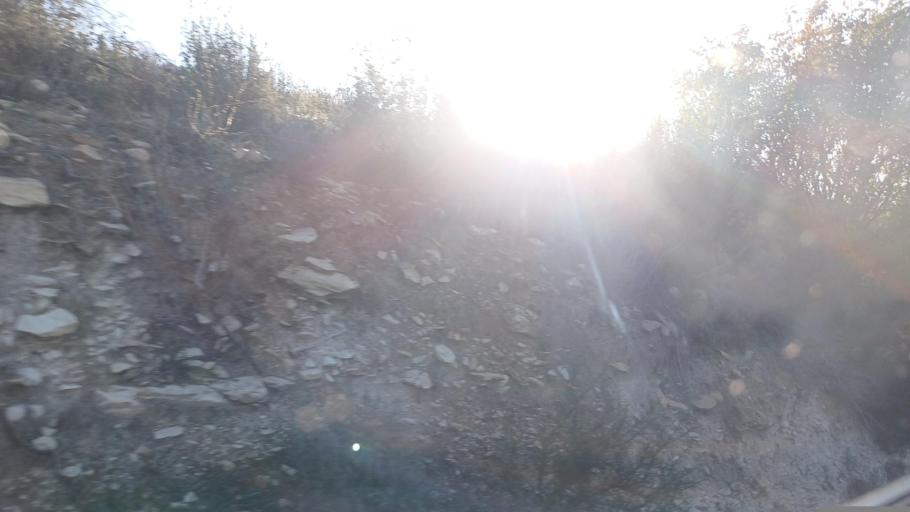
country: CY
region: Larnaka
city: Kofinou
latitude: 34.8397
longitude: 33.3049
